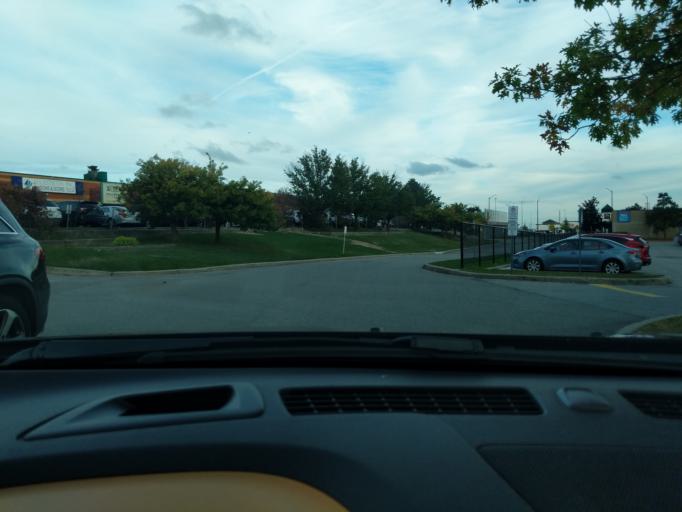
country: CA
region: Ontario
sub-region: York
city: Richmond Hill
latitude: 43.8488
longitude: -79.3775
